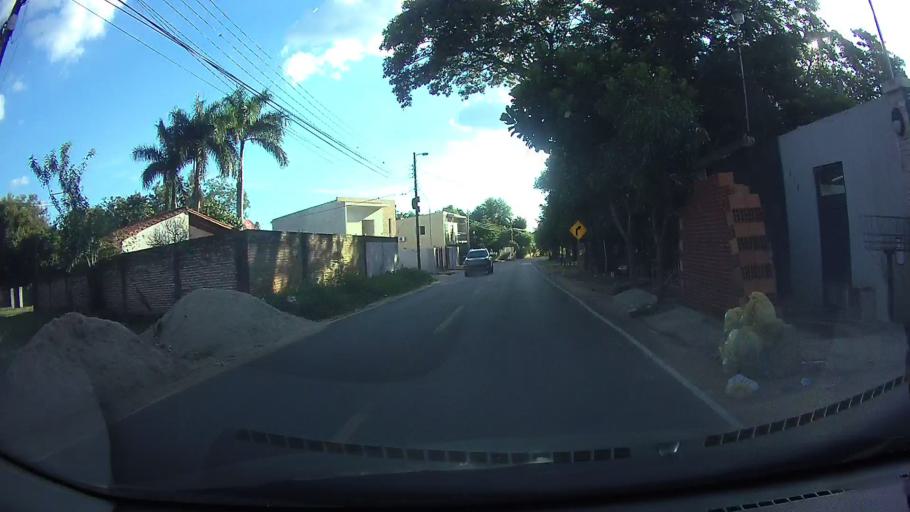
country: PY
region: Central
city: San Lorenzo
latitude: -25.2866
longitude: -57.5055
